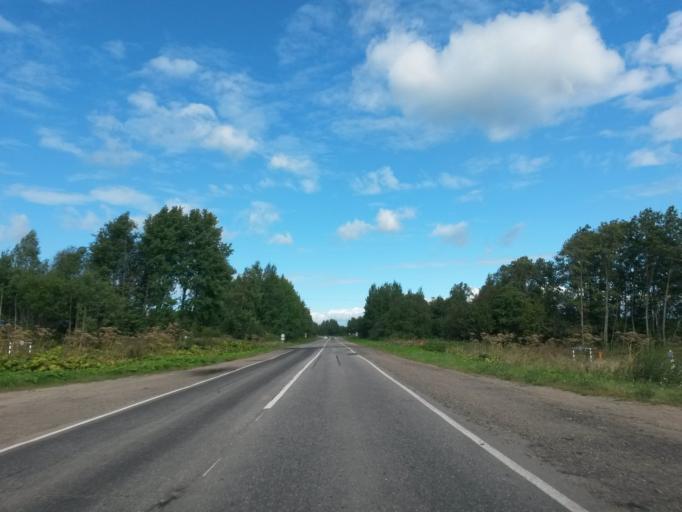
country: RU
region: Jaroslavl
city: Yaroslavl
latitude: 57.5321
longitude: 39.8744
